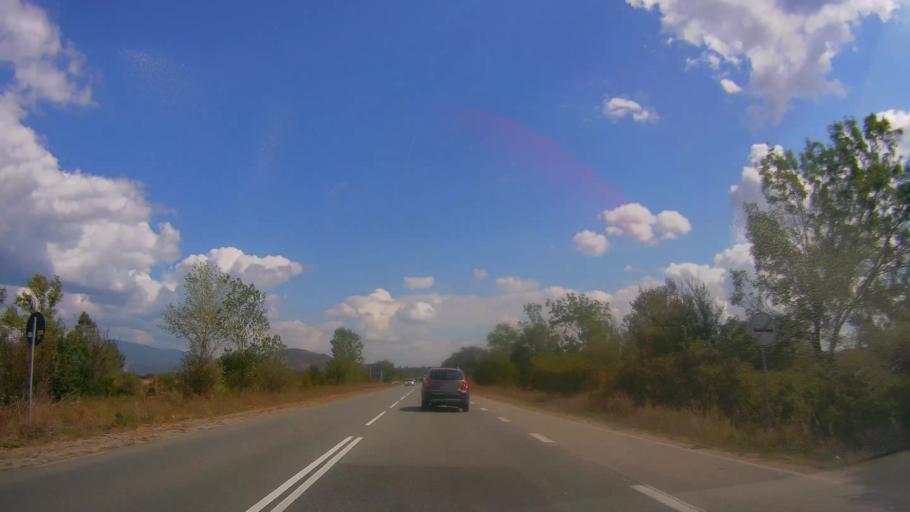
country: BG
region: Sliven
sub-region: Obshtina Tvurditsa
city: Tvurditsa
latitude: 42.6510
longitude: 25.9783
